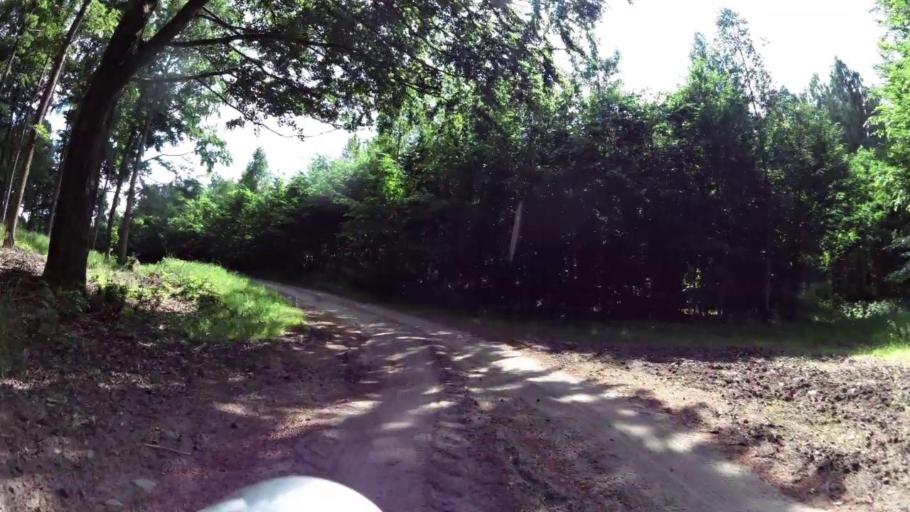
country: PL
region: West Pomeranian Voivodeship
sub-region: Powiat koszalinski
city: Bobolice
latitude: 53.9559
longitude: 16.6776
